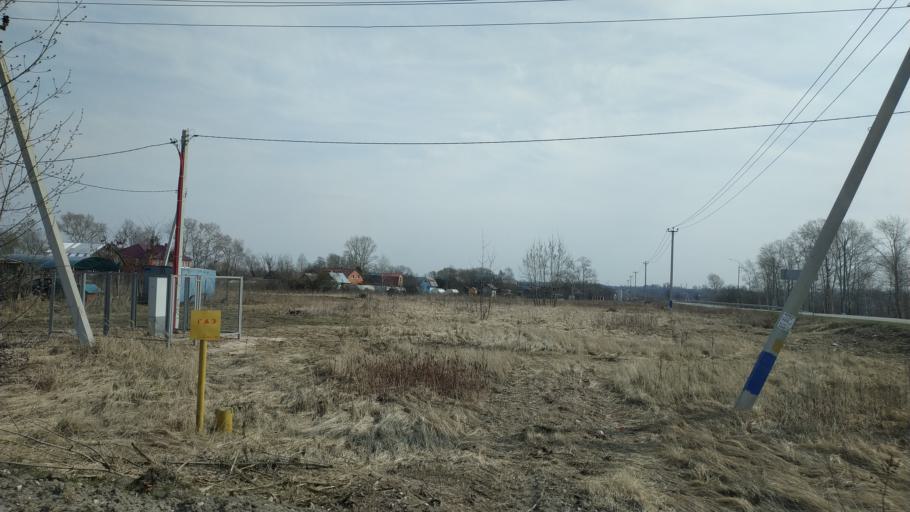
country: RU
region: Moskovskaya
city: Troitskoye
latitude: 55.3559
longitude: 38.5641
